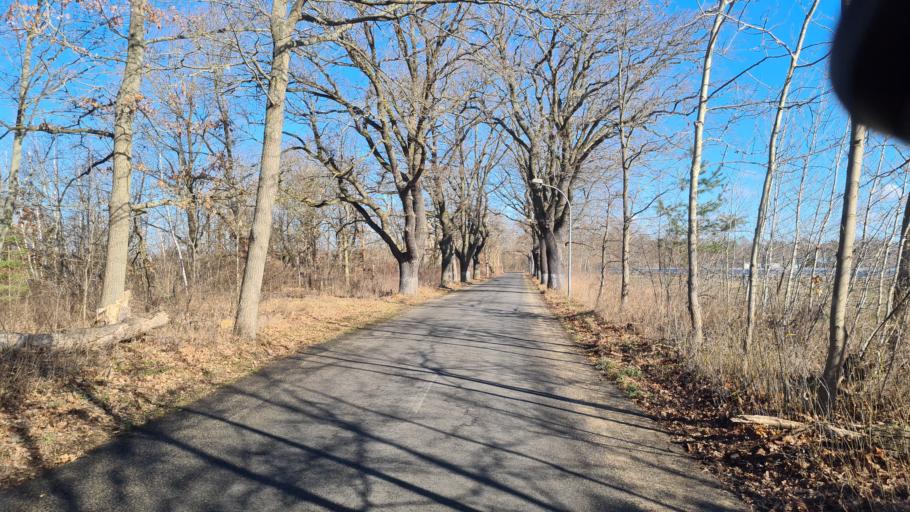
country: DE
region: Brandenburg
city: Falkenberg
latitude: 51.5524
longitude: 13.2159
